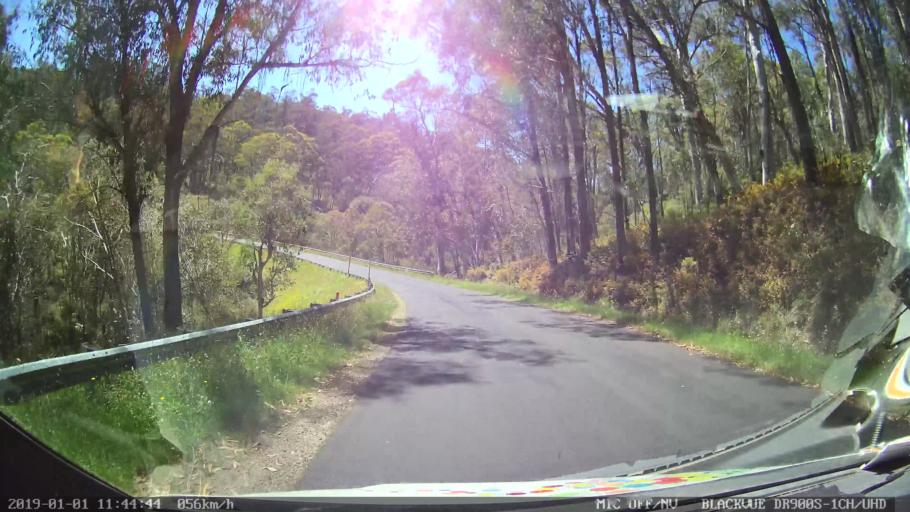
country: AU
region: New South Wales
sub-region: Snowy River
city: Jindabyne
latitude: -35.9010
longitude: 148.3949
